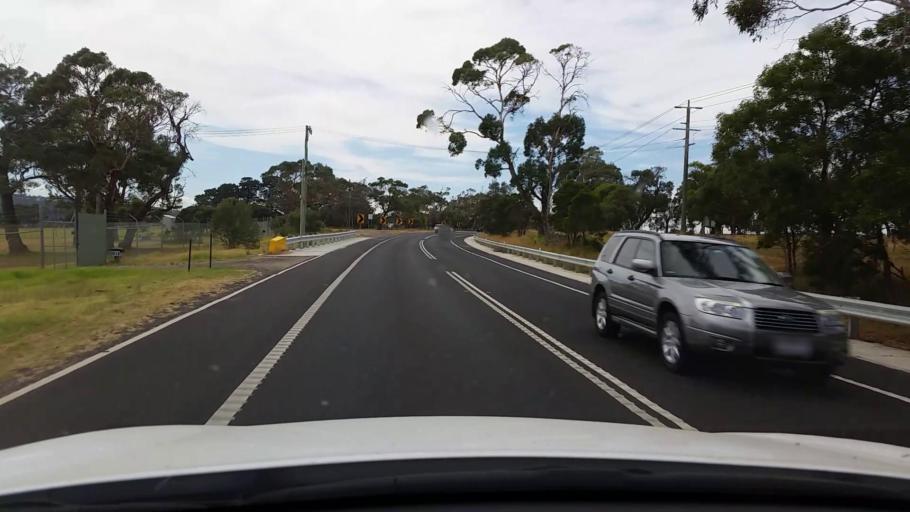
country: AU
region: Victoria
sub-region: Mornington Peninsula
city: Safety Beach
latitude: -38.3166
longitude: 145.0180
